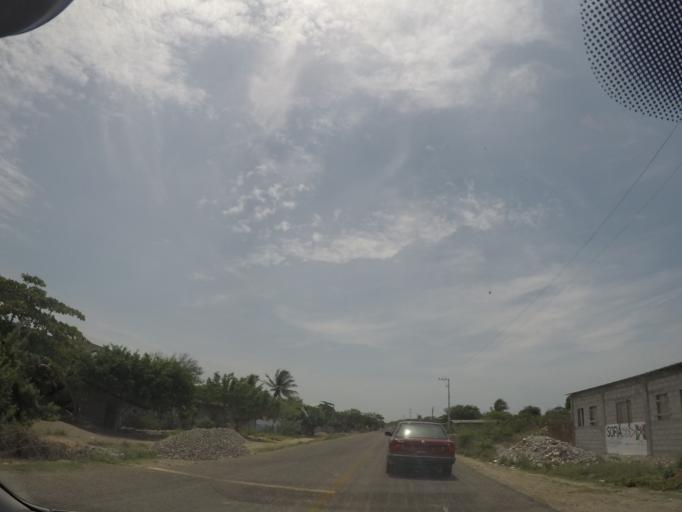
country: MX
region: Oaxaca
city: San Mateo del Mar
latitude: 16.2079
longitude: -95.0043
